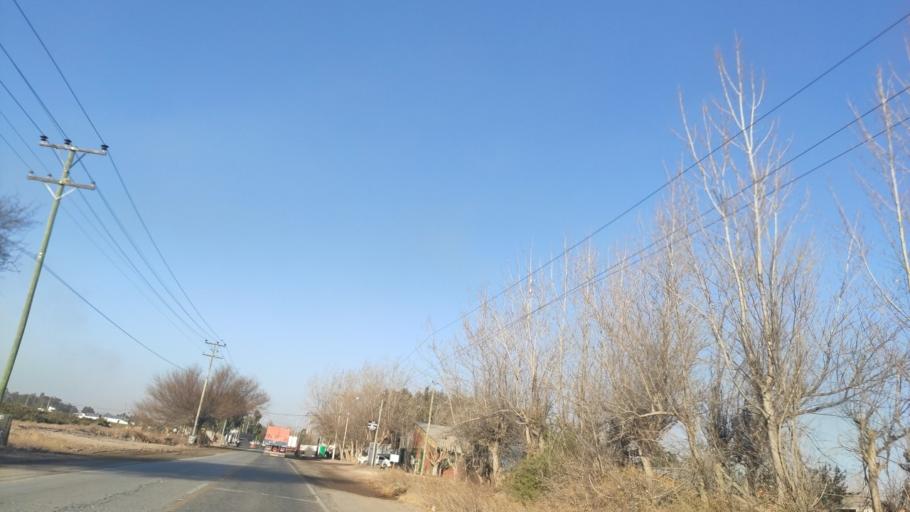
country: AR
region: San Juan
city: Villa Media Agua
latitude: -31.9794
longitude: -68.4427
